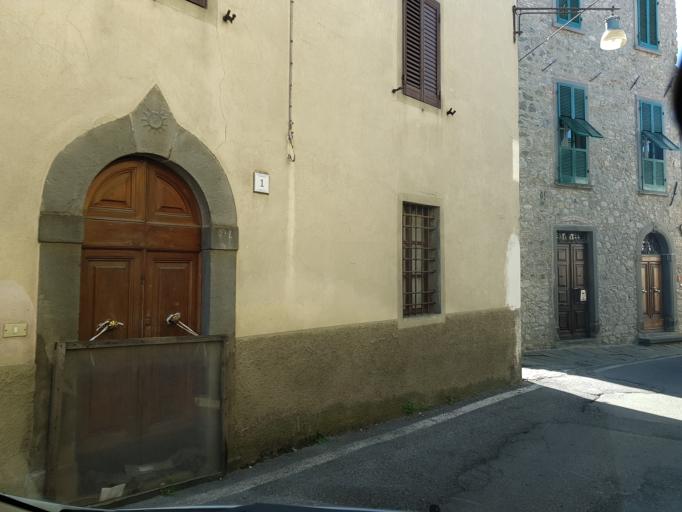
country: IT
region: Tuscany
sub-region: Provincia di Lucca
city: Camporgiano
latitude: 44.1585
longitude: 10.3357
